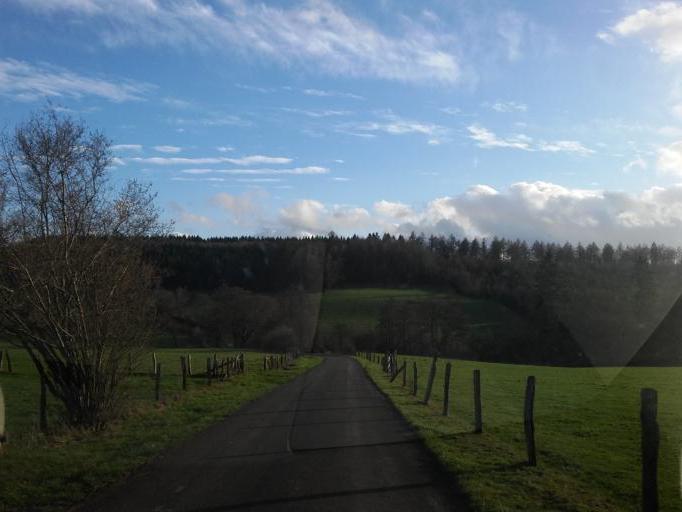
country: BE
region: Wallonia
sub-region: Province du Luxembourg
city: Neufchateau
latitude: 49.8080
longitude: 5.4428
